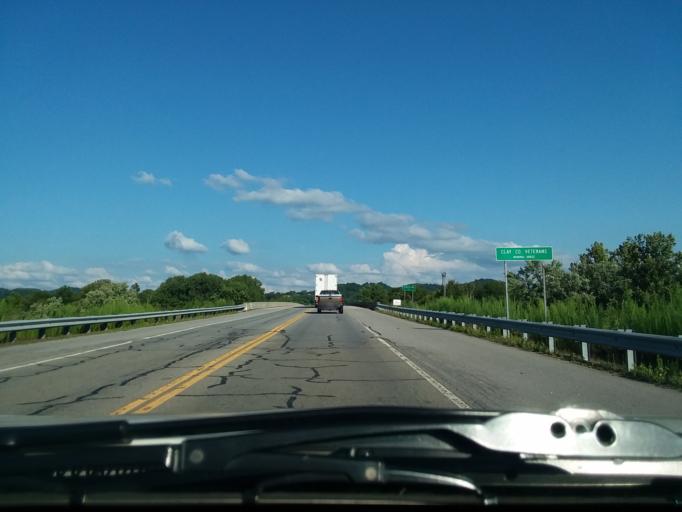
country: US
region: Tennessee
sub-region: Clay County
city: Celina
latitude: 36.5549
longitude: -85.5158
